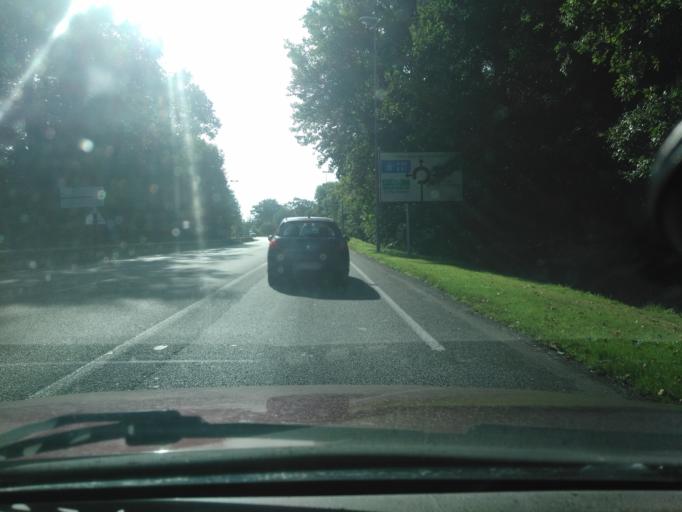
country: FR
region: Pays de la Loire
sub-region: Departement de la Vendee
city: La Roche-sur-Yon
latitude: 46.6701
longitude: -1.4125
